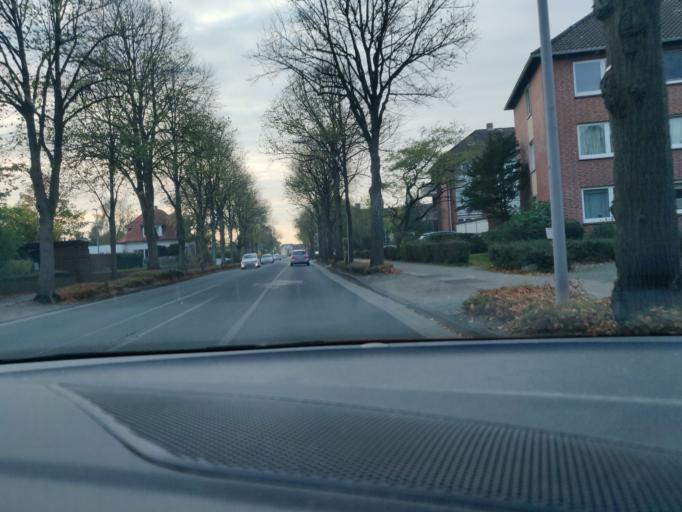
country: DE
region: Lower Saxony
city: Cuxhaven
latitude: 53.8595
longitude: 8.6859
